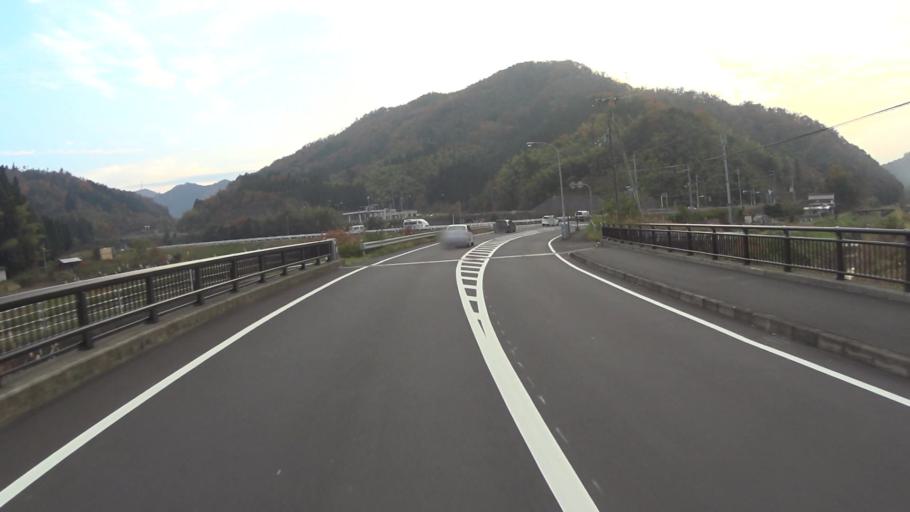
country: JP
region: Kyoto
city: Maizuru
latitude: 35.4631
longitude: 135.4222
